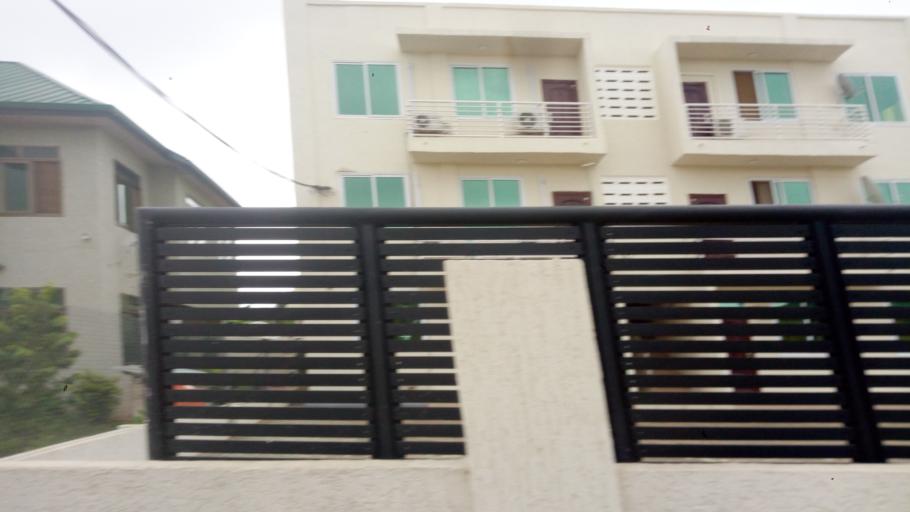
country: GH
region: Greater Accra
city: Achiaman
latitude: 5.7264
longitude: -0.3153
